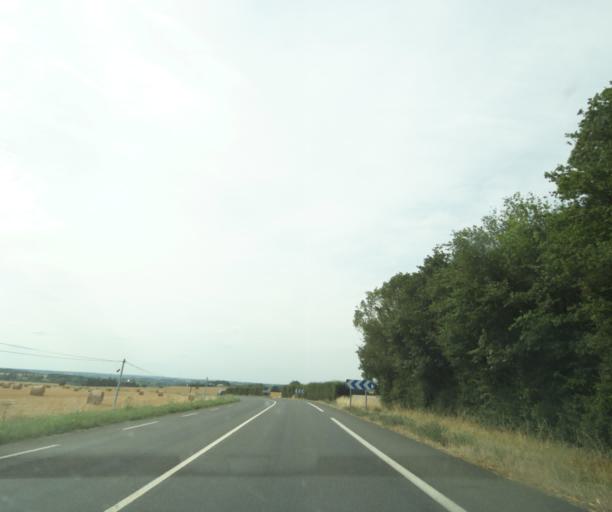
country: FR
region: Centre
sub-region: Departement d'Indre-et-Loire
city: Saint-Christophe-sur-le-Nais
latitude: 47.6532
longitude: 0.4906
